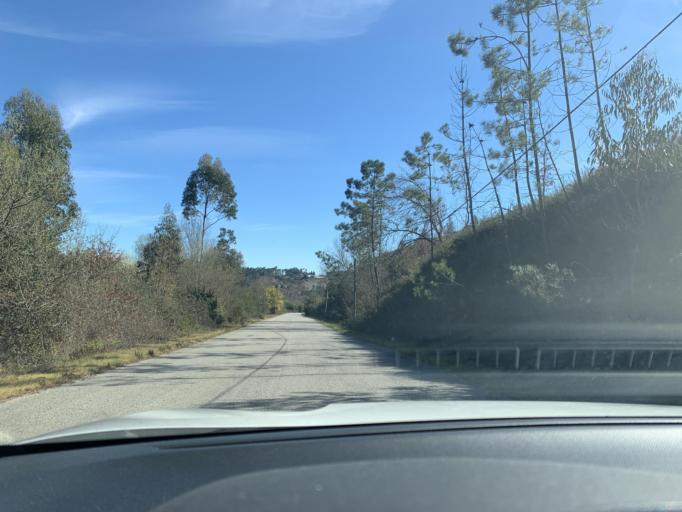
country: PT
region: Viseu
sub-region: Concelho de Tondela
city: Tondela
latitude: 40.6025
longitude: -8.0308
